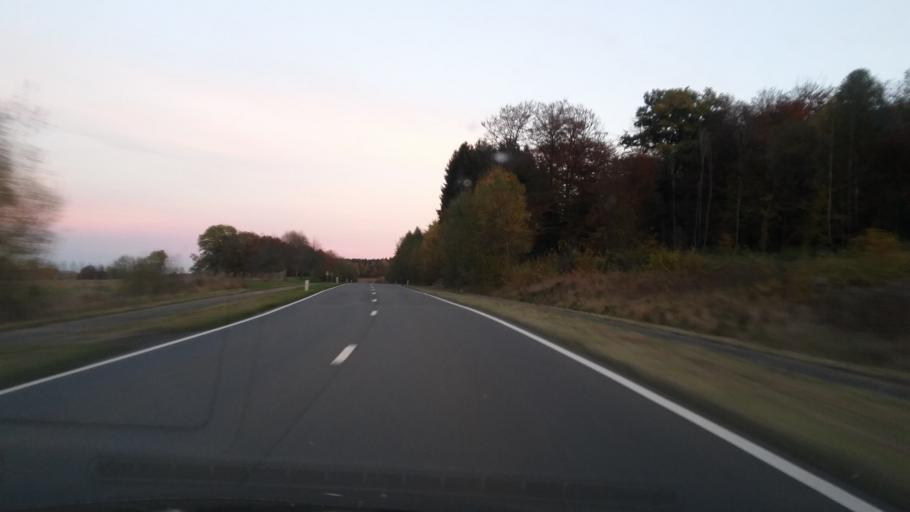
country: BE
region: Wallonia
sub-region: Province du Luxembourg
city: Tintigny
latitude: 49.6888
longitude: 5.4586
